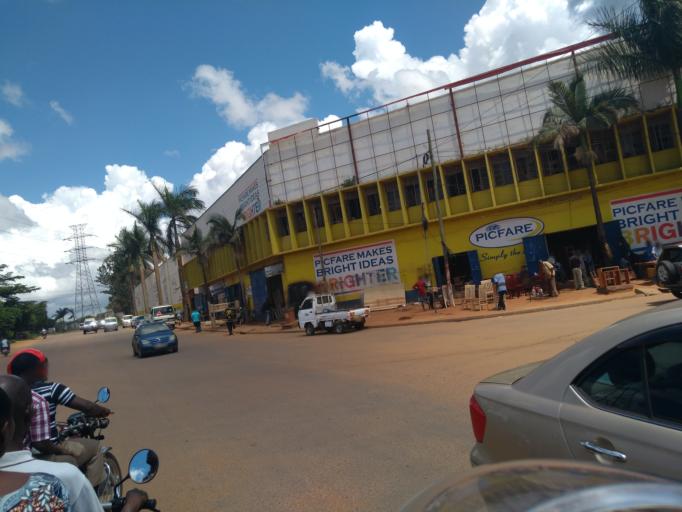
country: UG
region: Central Region
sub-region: Kampala District
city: Kampala
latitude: 0.3215
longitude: 32.6079
